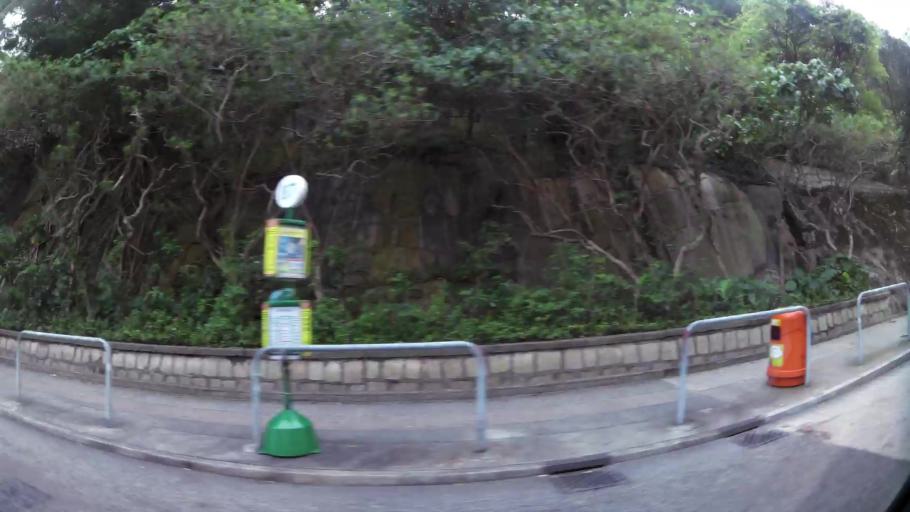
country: HK
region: Kowloon City
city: Kowloon
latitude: 22.3112
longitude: 114.2384
